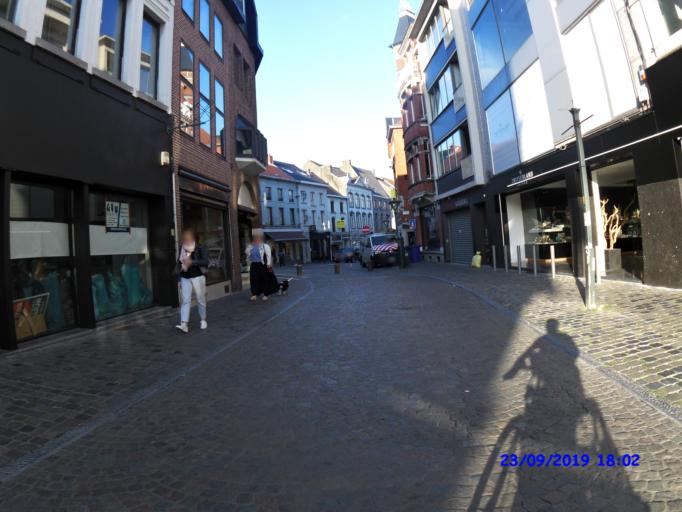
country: BE
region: Flanders
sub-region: Provincie Oost-Vlaanderen
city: Aalst
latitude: 50.9386
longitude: 4.0399
